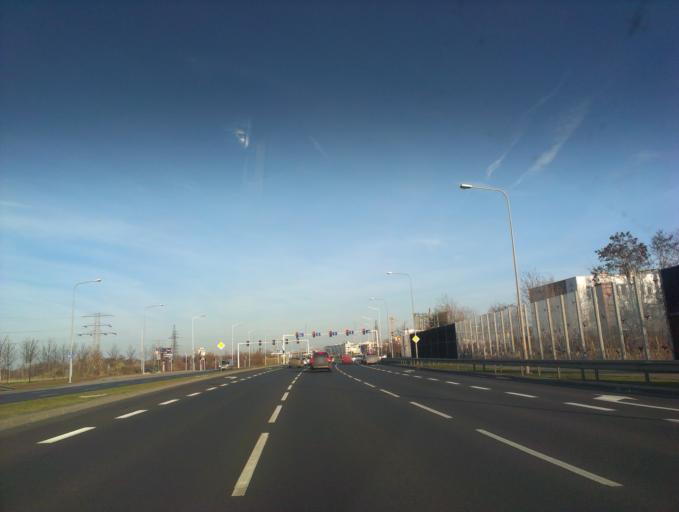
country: PL
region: Greater Poland Voivodeship
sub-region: Poznan
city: Poznan
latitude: 52.4187
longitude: 16.9600
